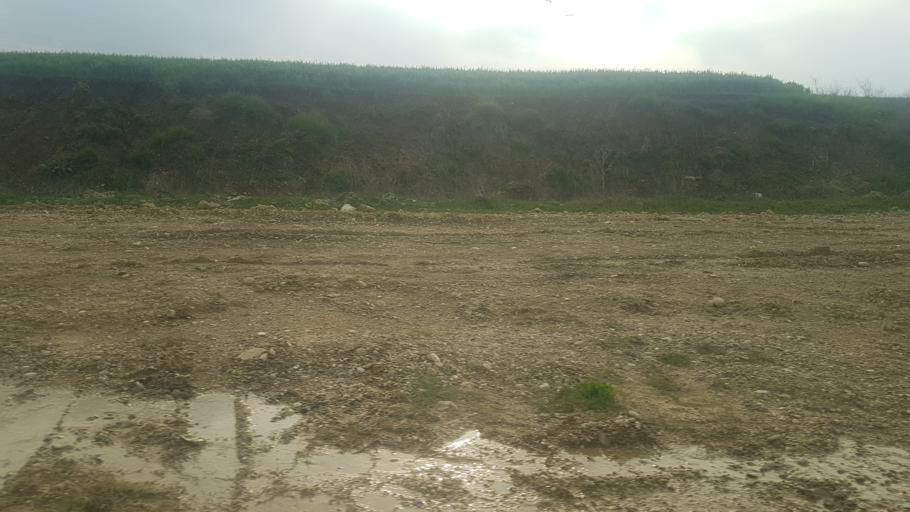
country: TR
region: Adana
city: Seyhan
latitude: 37.0481
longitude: 35.2103
